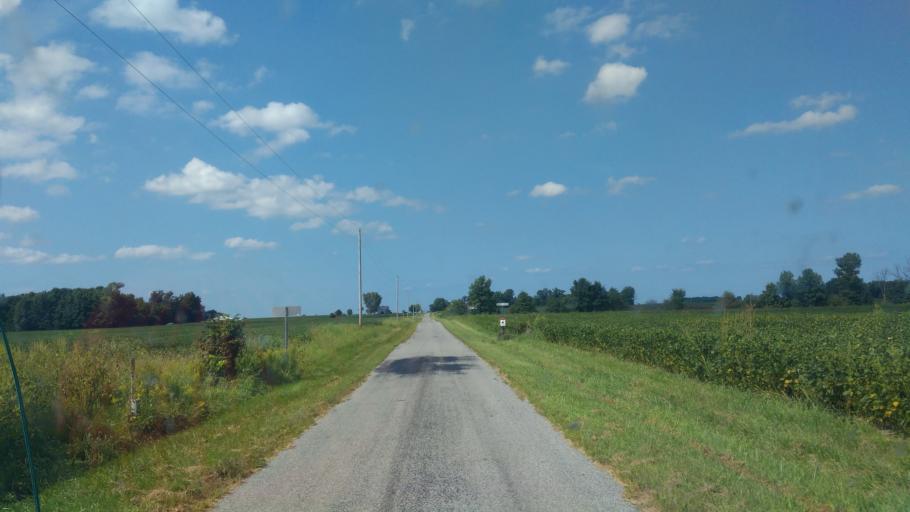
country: US
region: Ohio
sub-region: Union County
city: Richwood
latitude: 40.5044
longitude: -83.4502
